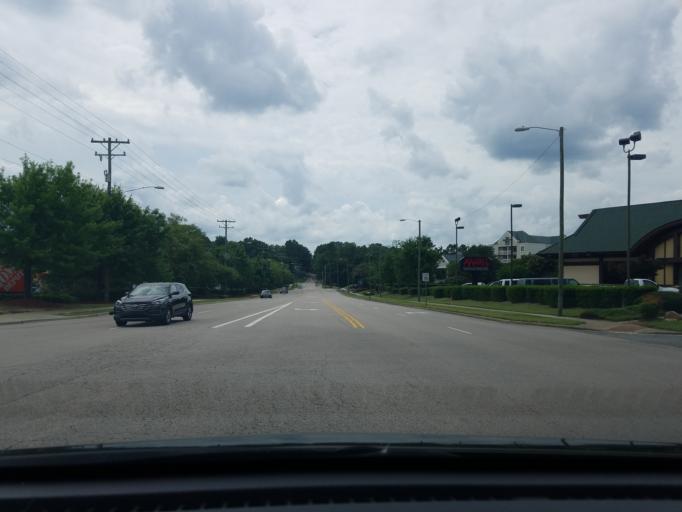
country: US
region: North Carolina
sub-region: Orange County
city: Chapel Hill
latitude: 35.9515
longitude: -78.9944
